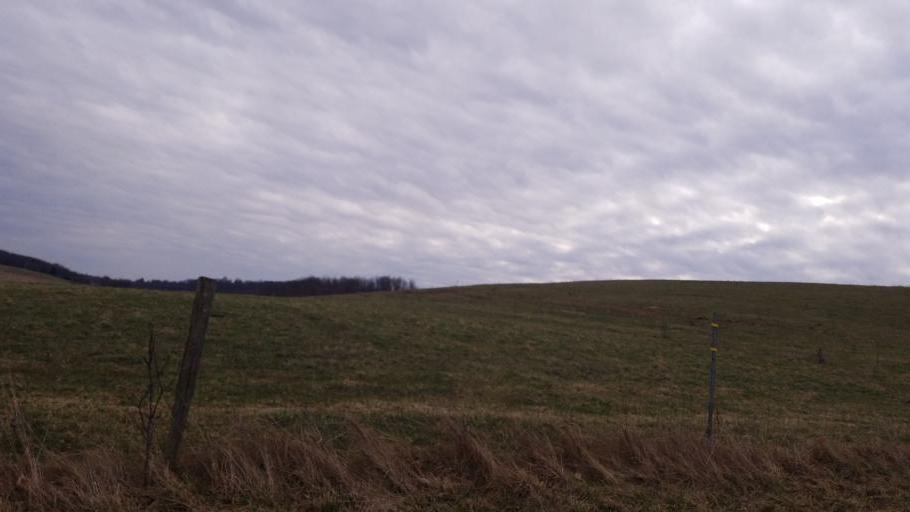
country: US
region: Ohio
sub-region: Knox County
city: Fredericktown
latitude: 40.5185
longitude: -82.4706
